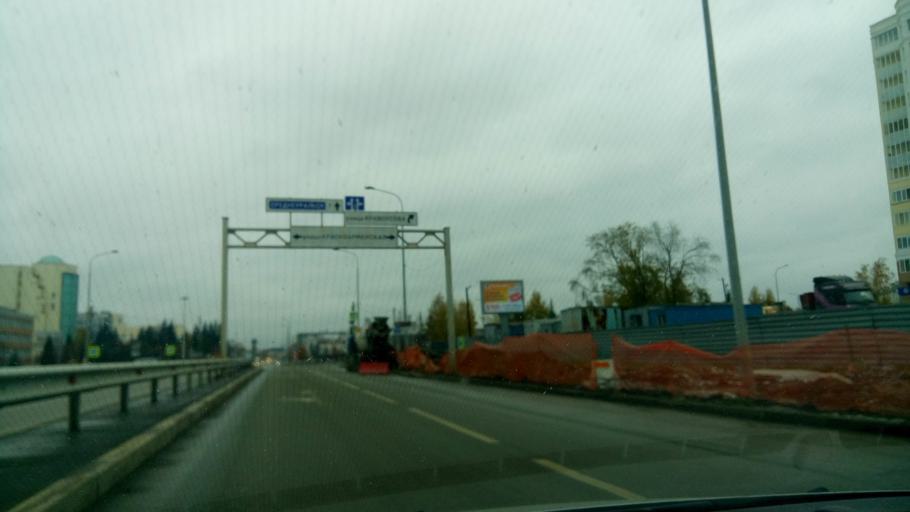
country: RU
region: Sverdlovsk
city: Verkhnyaya Pyshma
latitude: 56.9648
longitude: 60.5812
